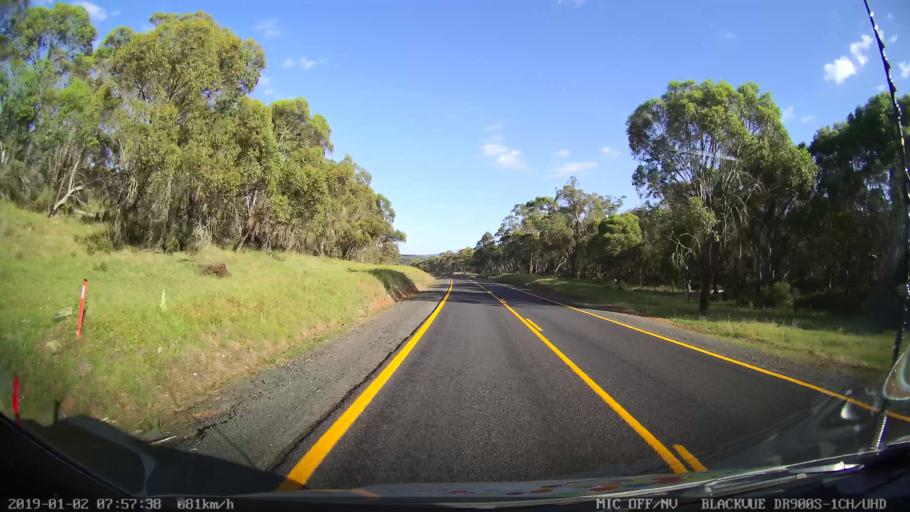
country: AU
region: New South Wales
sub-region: Tumut Shire
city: Tumut
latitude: -35.6616
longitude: 148.4727
